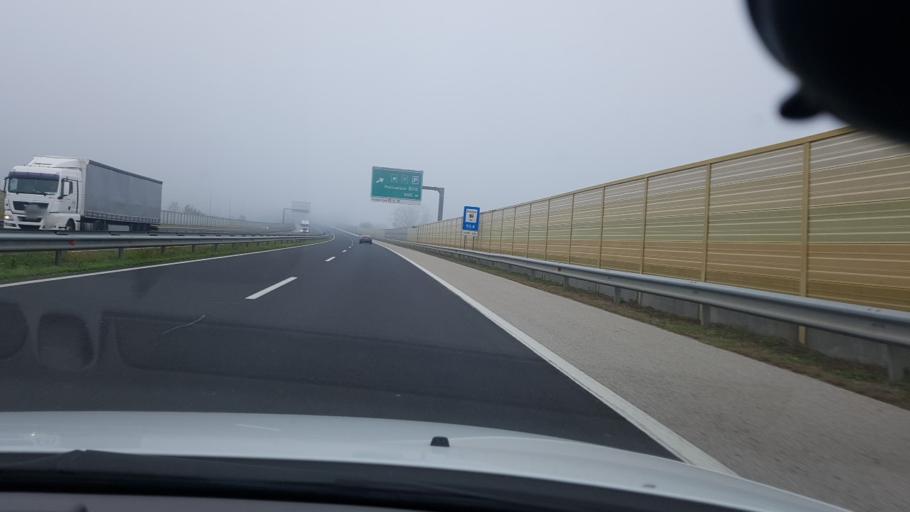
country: SI
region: Brezice
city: Brezice
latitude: 45.8901
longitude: 15.6090
